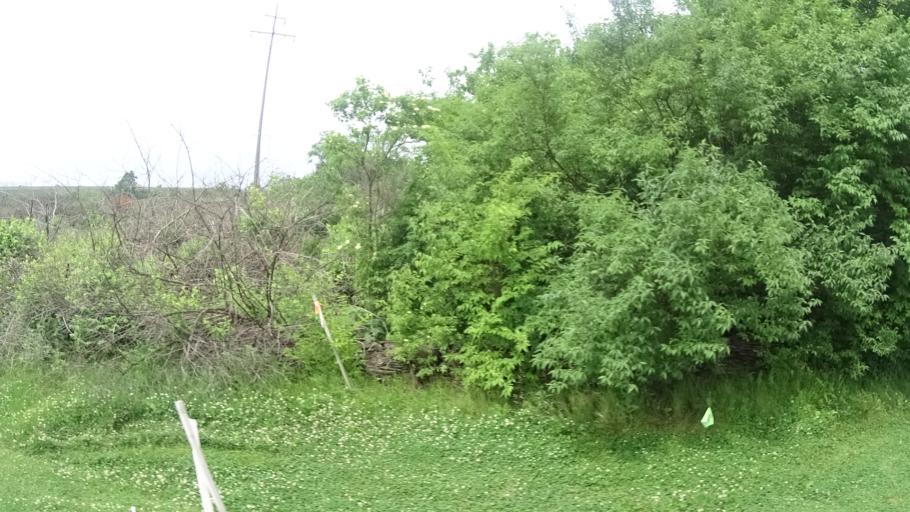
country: US
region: Ohio
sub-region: Huron County
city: Bellevue
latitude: 41.3470
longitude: -82.7855
